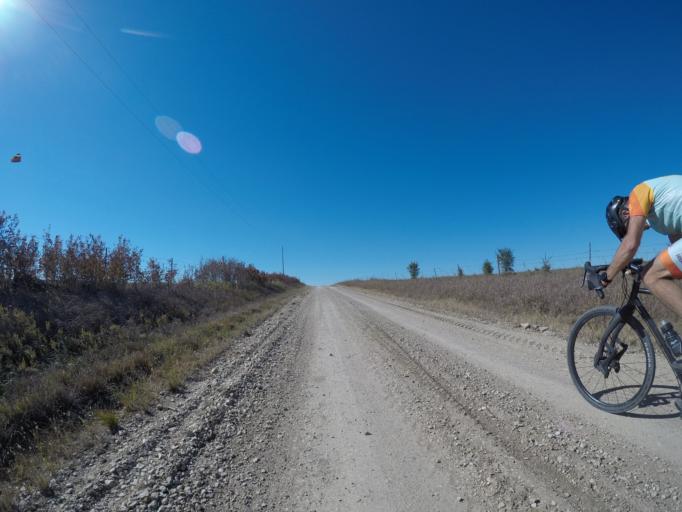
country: US
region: Kansas
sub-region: Wabaunsee County
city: Alma
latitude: 39.0290
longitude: -96.3817
